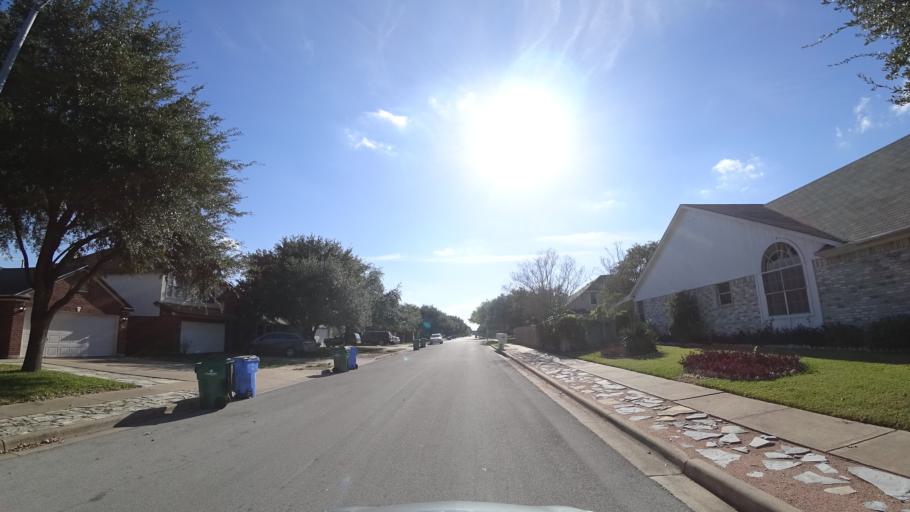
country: US
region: Texas
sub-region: Travis County
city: Wells Branch
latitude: 30.4616
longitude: -97.6853
